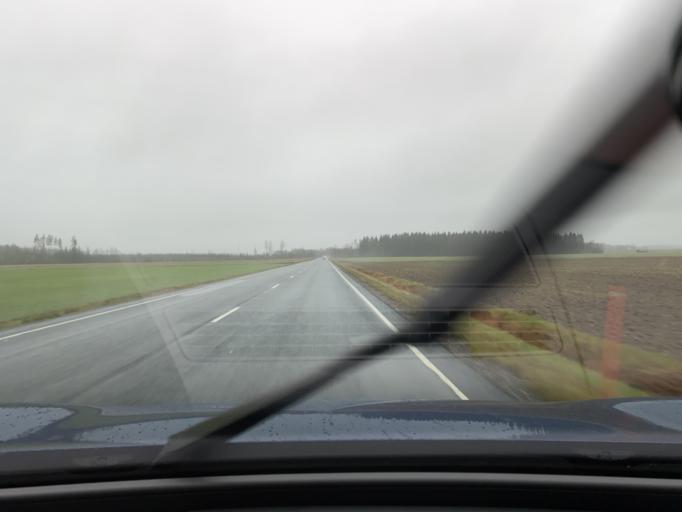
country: FI
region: Varsinais-Suomi
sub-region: Loimaa
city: Alastaro
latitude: 60.9058
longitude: 22.9272
